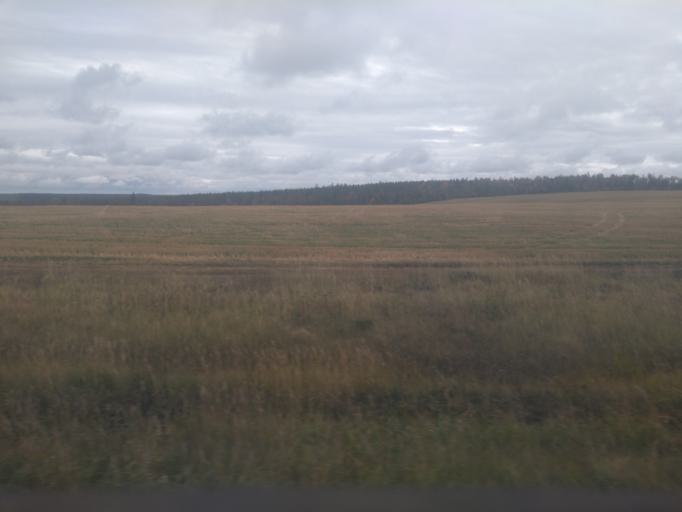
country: RU
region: Udmurtiya
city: Alnashi
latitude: 56.1387
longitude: 52.5674
